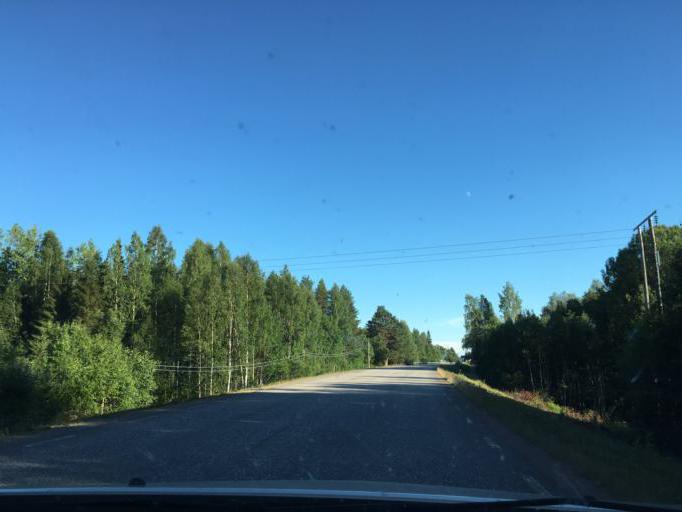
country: SE
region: Norrbotten
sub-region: Kalix Kommun
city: Rolfs
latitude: 65.9087
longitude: 22.9294
